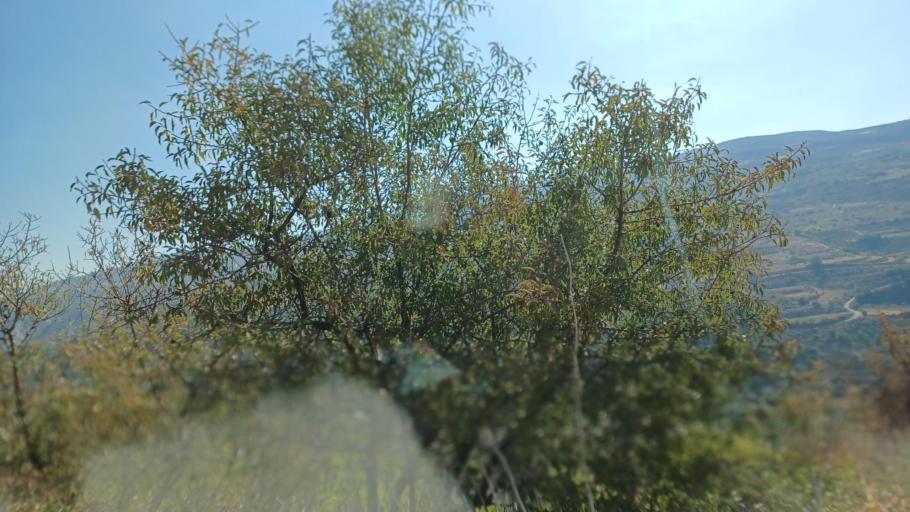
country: CY
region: Limassol
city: Pachna
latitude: 34.8422
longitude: 32.7166
